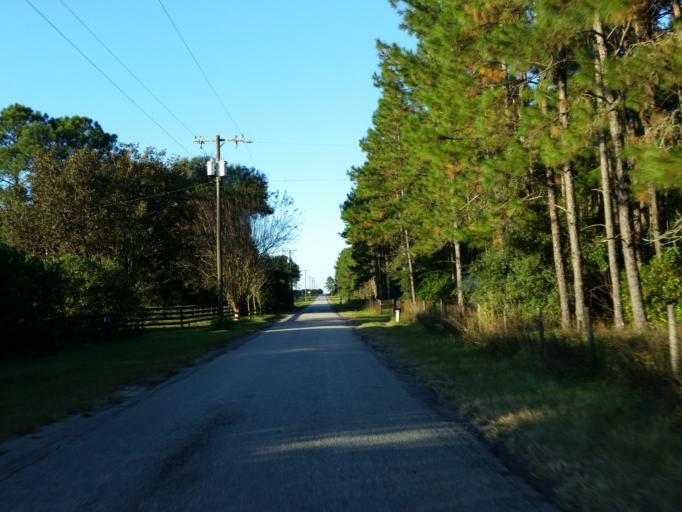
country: US
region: Florida
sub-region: Pasco County
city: Dade City North
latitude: 28.4224
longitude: -82.2616
